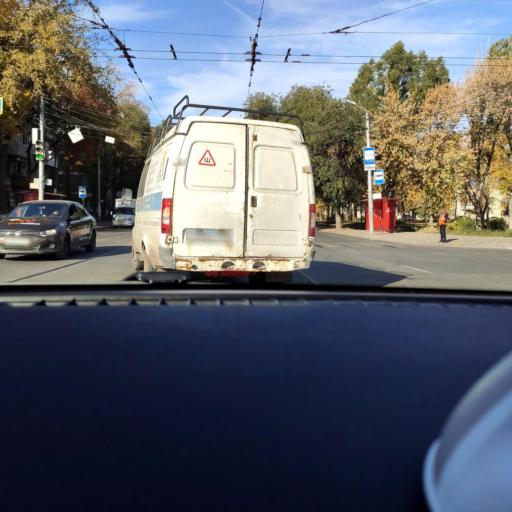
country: RU
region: Samara
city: Petra-Dubrava
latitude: 53.2398
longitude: 50.2801
